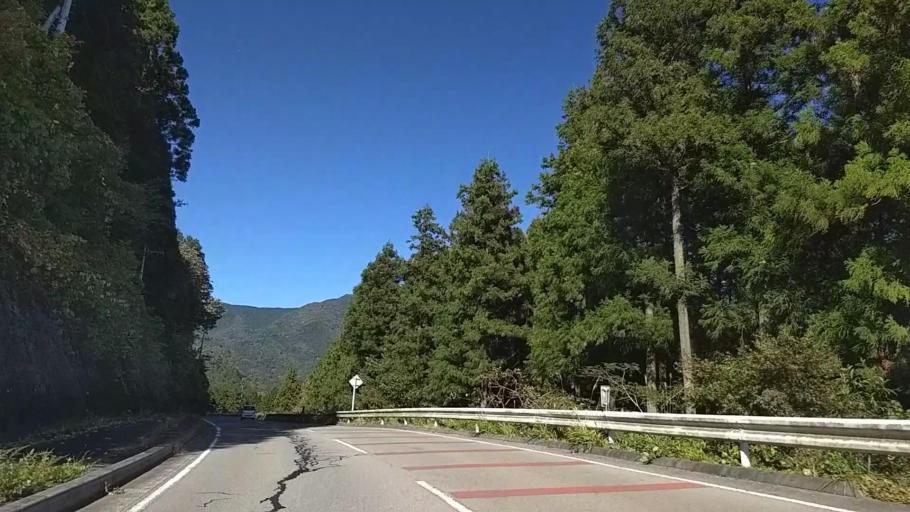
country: JP
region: Yamanashi
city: Uenohara
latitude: 35.6588
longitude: 139.0930
